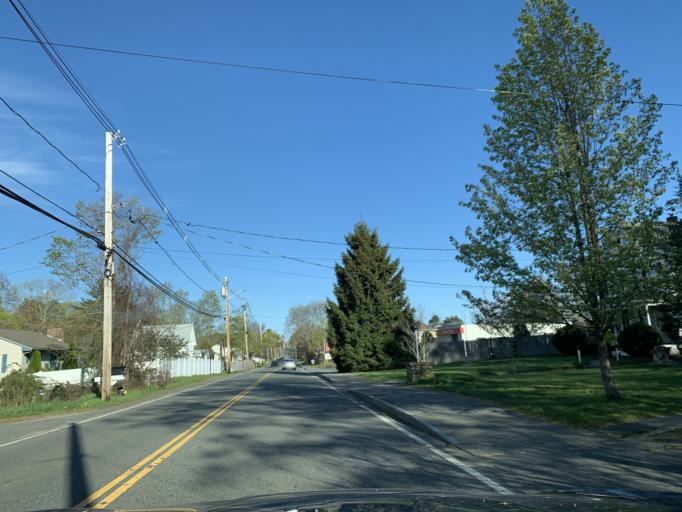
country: US
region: Massachusetts
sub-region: Norfolk County
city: Stoughton
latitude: 42.1292
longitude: -71.1205
